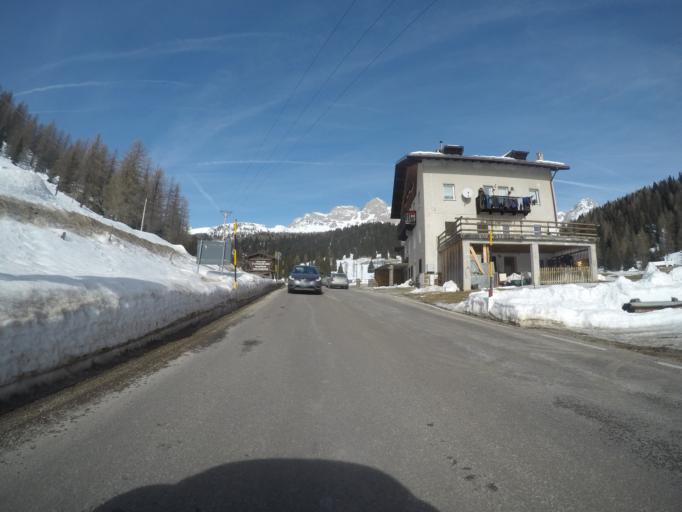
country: IT
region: Veneto
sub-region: Provincia di Belluno
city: Falcade Alto
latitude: 46.3760
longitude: 11.8208
